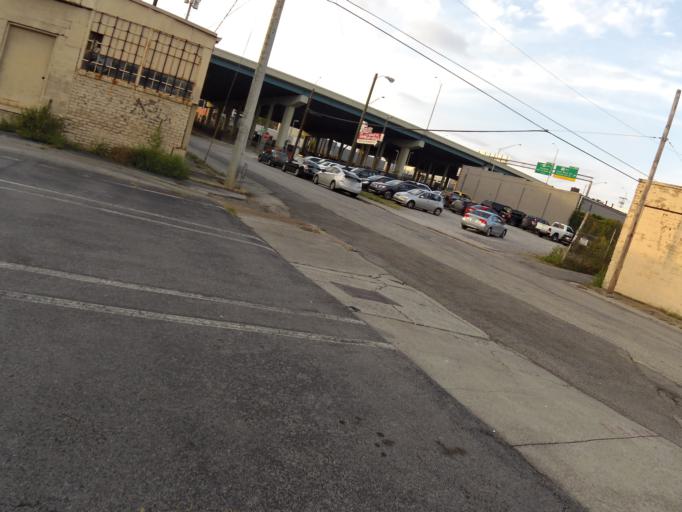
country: US
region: Tennessee
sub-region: Knox County
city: Knoxville
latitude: 35.9710
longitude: -83.9211
